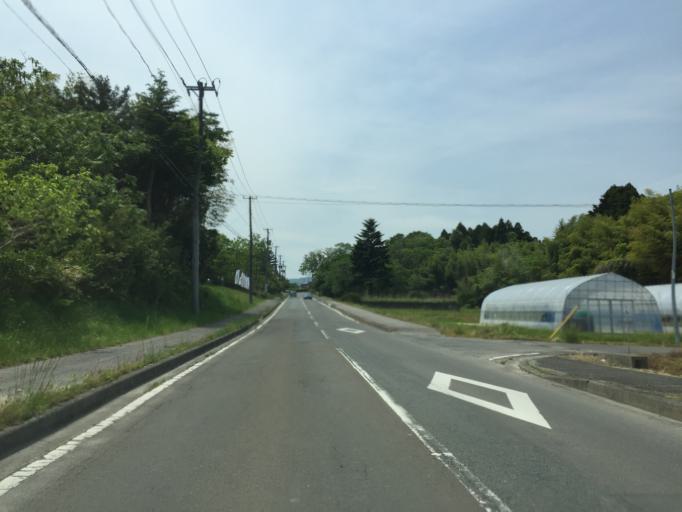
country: JP
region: Miyagi
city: Marumori
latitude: 37.8161
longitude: 140.9323
